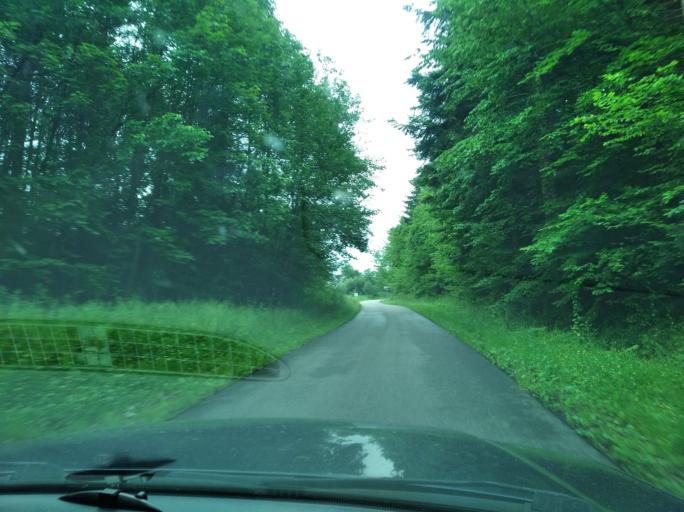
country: PL
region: Subcarpathian Voivodeship
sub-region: Powiat przemyski
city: Dubiecko
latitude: 49.8705
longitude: 22.4053
